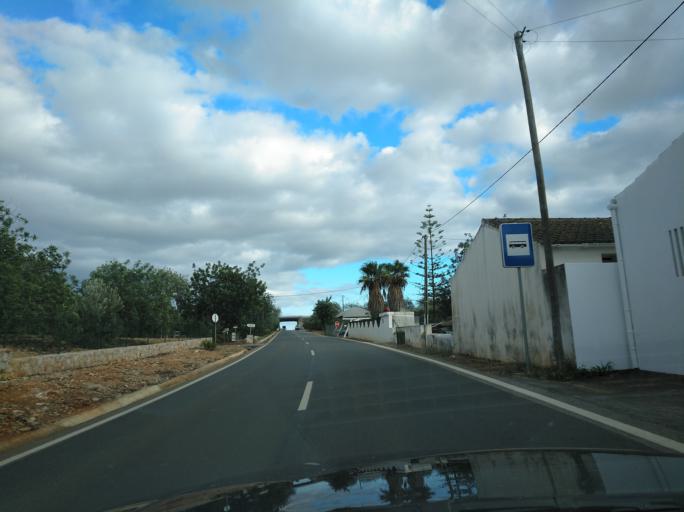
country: PT
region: Faro
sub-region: Tavira
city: Luz
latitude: 37.1371
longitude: -7.7019
